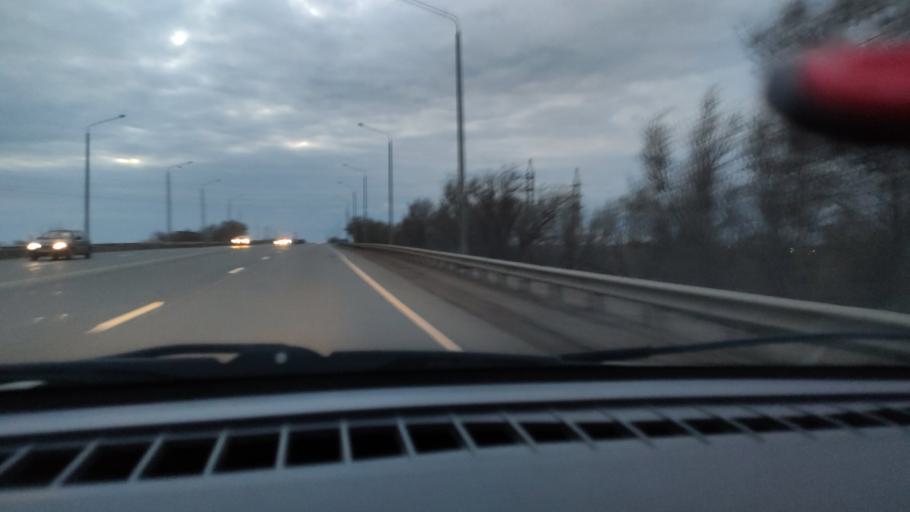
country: RU
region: Orenburg
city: Orenburg
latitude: 51.8514
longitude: 55.1415
